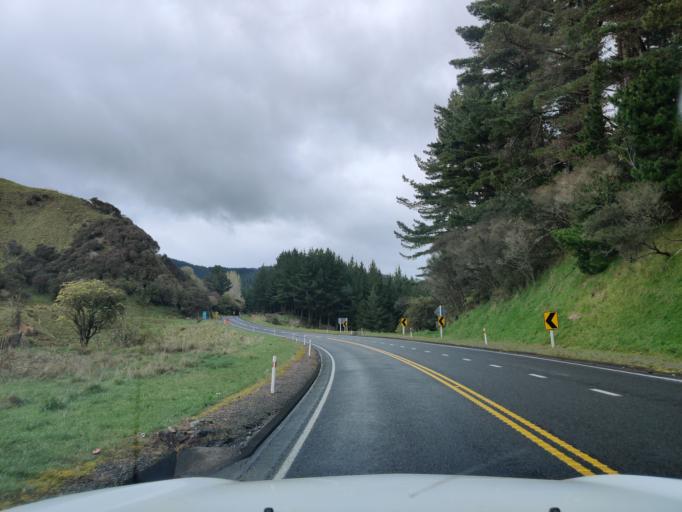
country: NZ
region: Waikato
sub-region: Otorohanga District
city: Otorohanga
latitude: -38.6435
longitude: 175.2056
